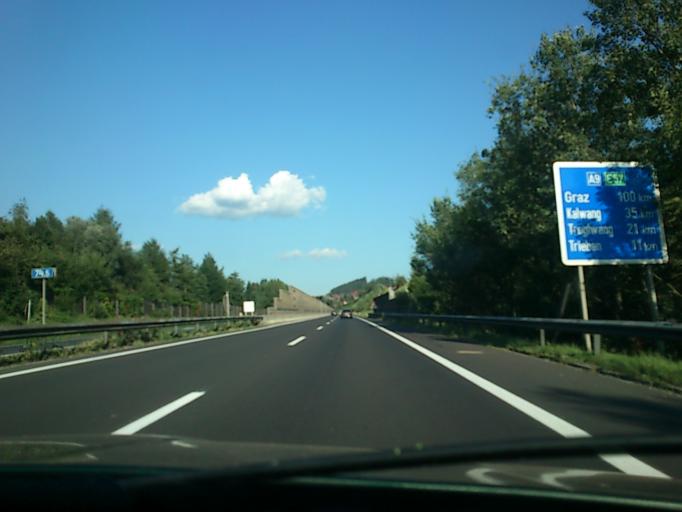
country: AT
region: Styria
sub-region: Politischer Bezirk Liezen
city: Rottenmann
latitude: 47.5235
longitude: 14.3439
